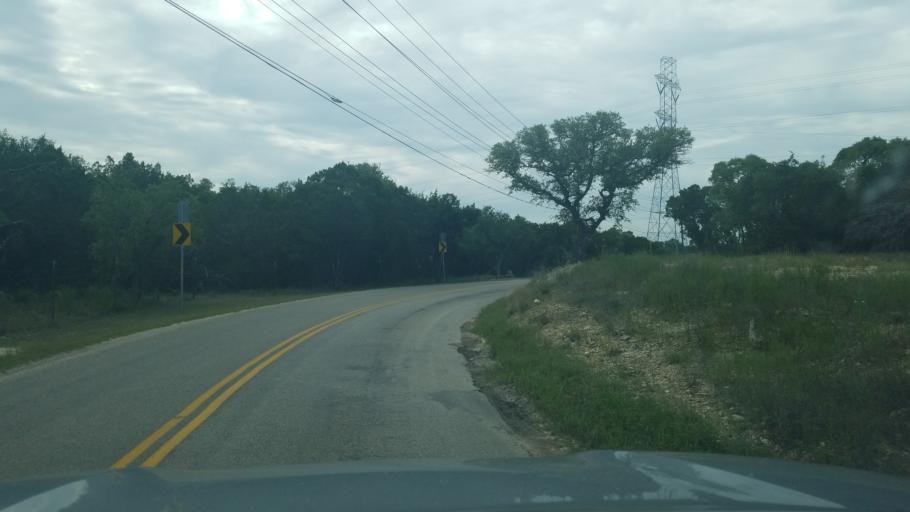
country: US
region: Texas
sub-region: Comal County
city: Bulverde
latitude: 29.7783
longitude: -98.4129
